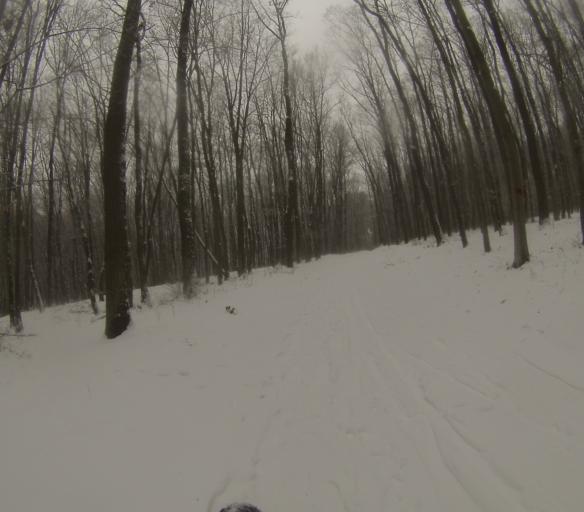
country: CZ
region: South Moravian
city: Strelice
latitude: 49.1382
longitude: 16.4905
